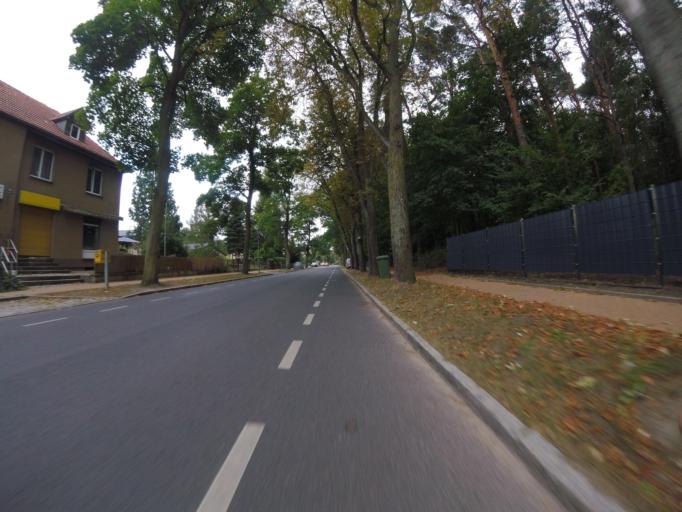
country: DE
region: Brandenburg
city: Birkenwerder
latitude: 52.6761
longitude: 13.3128
